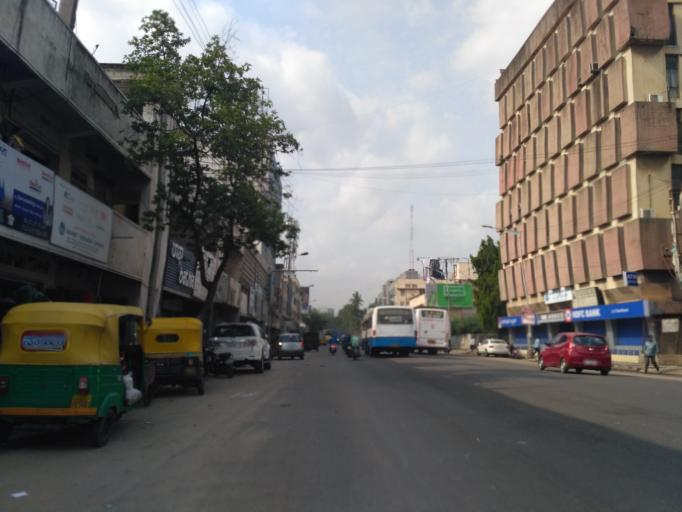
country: IN
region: Karnataka
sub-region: Bangalore Urban
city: Bangalore
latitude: 12.9594
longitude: 77.5829
